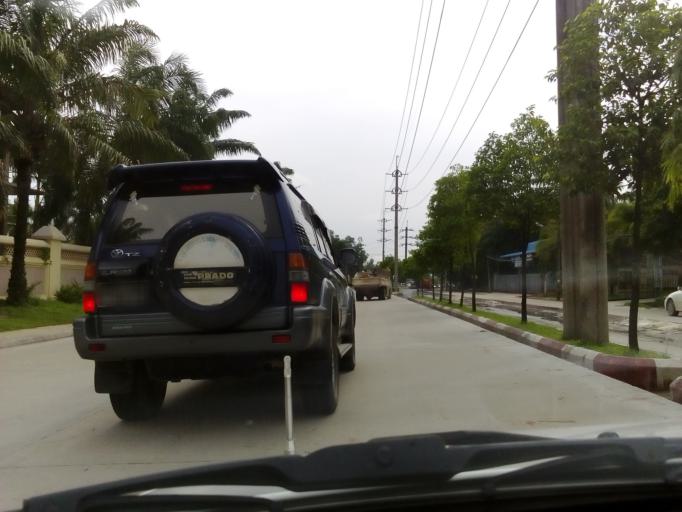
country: MM
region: Yangon
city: Yangon
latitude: 16.8671
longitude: 96.1341
